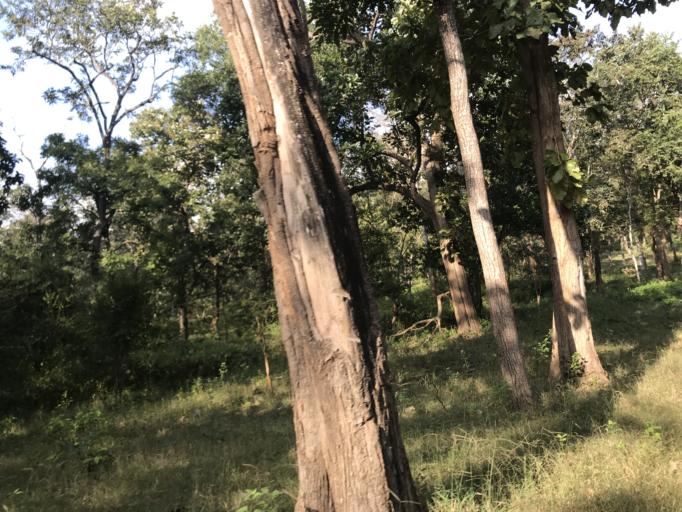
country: IN
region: Karnataka
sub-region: Mysore
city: Heggadadevankote
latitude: 11.9513
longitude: 76.1932
